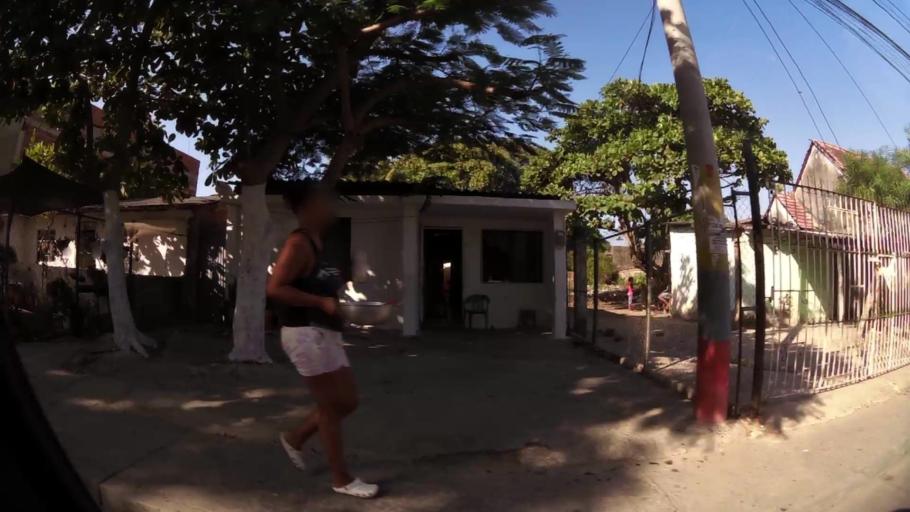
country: CO
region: Bolivar
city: Cartagena
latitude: 10.4080
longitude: -75.5045
